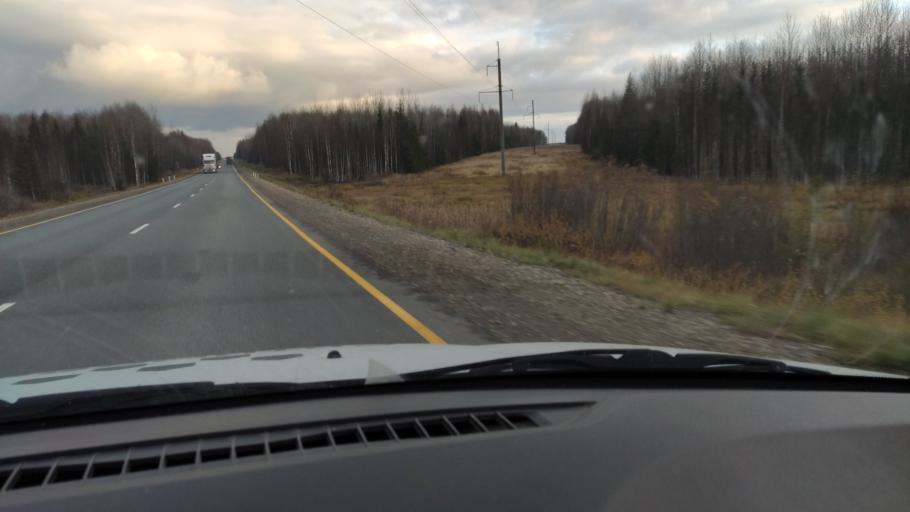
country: RU
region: Kirov
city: Chernaya Kholunitsa
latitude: 58.8064
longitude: 51.8467
